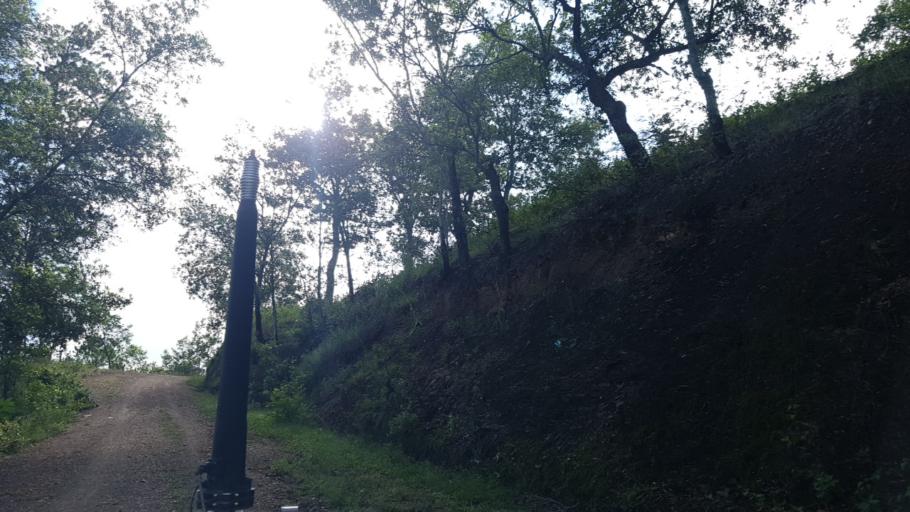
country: NI
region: Nueva Segovia
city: Ciudad Antigua
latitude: 13.6355
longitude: -86.2872
